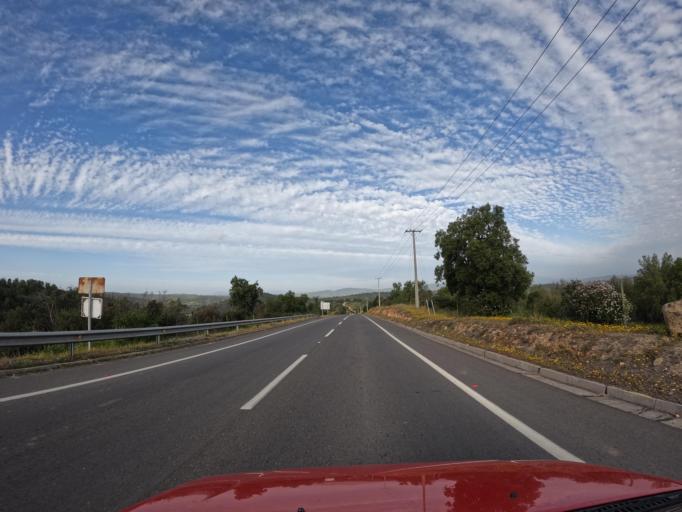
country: CL
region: Valparaiso
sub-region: San Antonio Province
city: San Antonio
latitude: -34.0501
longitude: -71.5976
